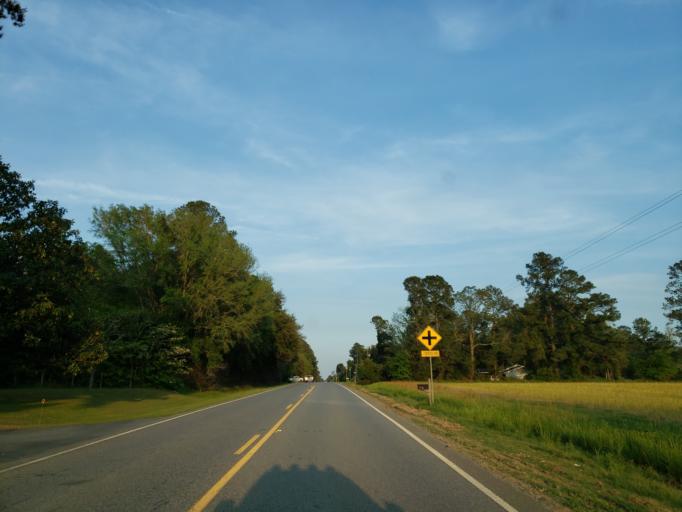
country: US
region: Georgia
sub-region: Lowndes County
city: Hahira
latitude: 30.9957
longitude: -83.4321
